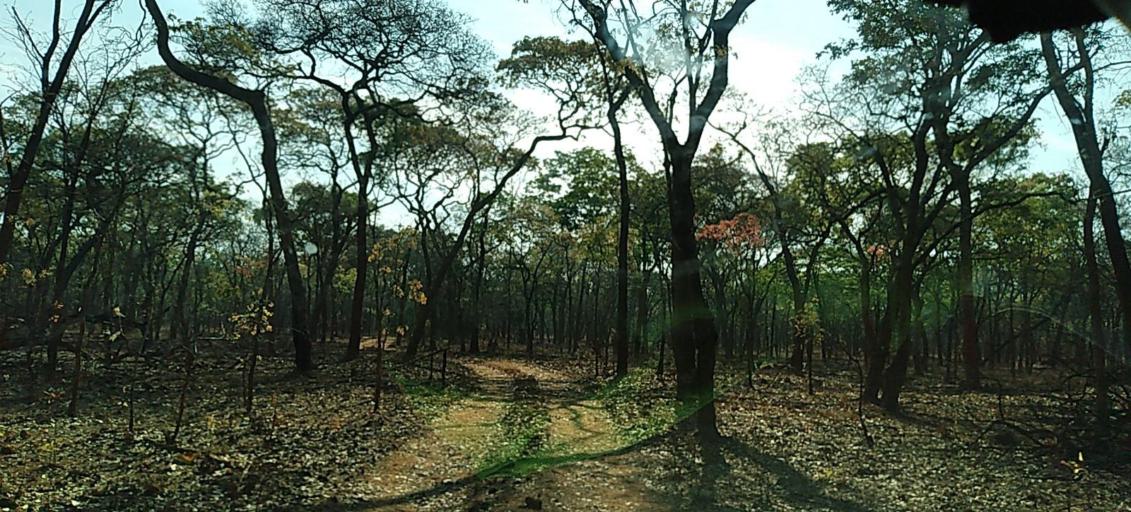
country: ZM
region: North-Western
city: Kalengwa
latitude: -13.2261
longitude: 25.0950
